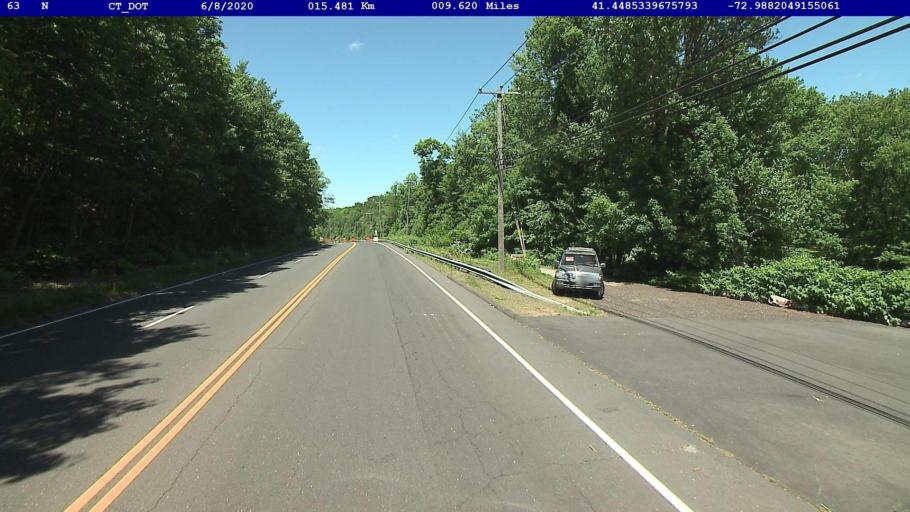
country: US
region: Connecticut
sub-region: New Haven County
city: Prospect
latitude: 41.4486
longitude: -72.9882
